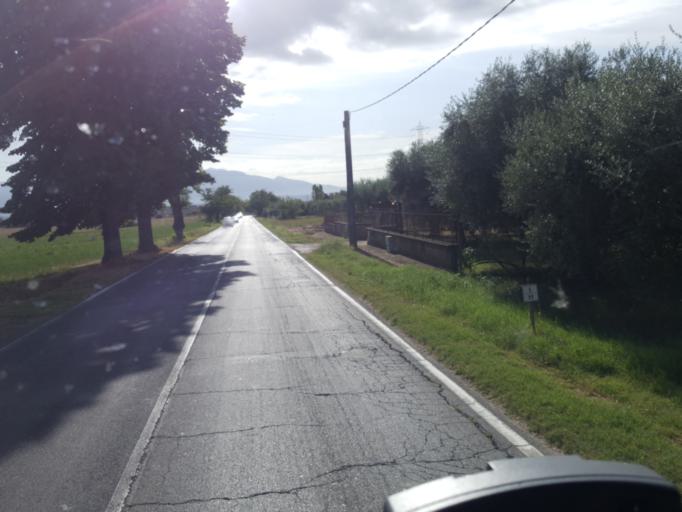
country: IT
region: Latium
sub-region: Citta metropolitana di Roma Capitale
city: Bivio di Capanelle
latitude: 42.1284
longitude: 12.5702
